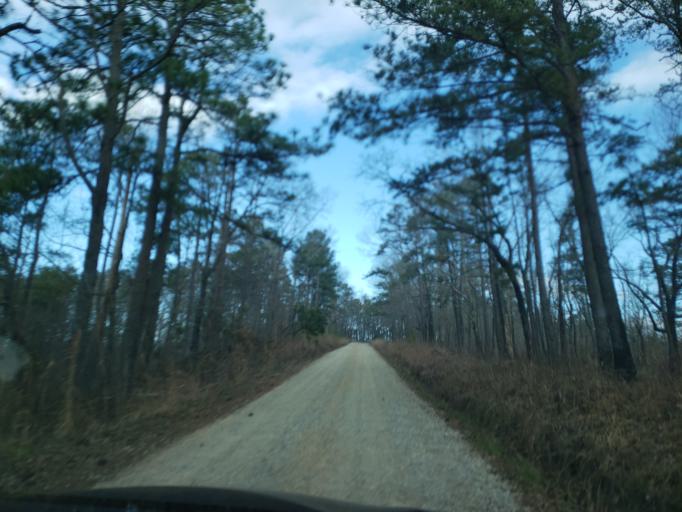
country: US
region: Alabama
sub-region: Cleburne County
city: Heflin
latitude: 33.6673
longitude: -85.6336
